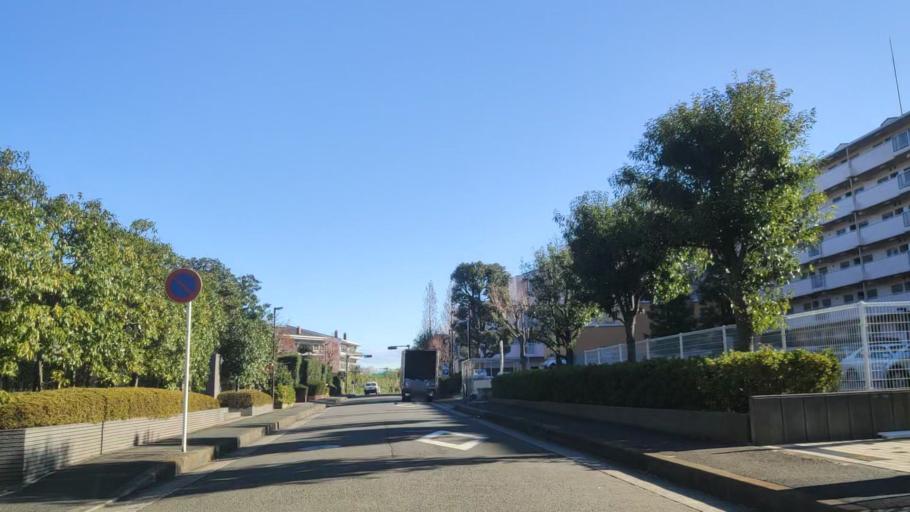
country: JP
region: Kanagawa
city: Yokohama
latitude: 35.4212
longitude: 139.6553
